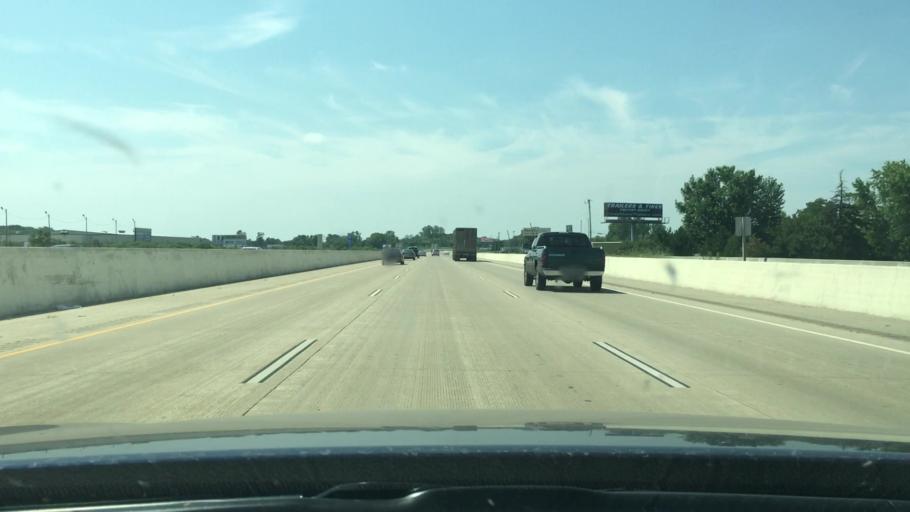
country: US
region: Wisconsin
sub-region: Winnebago County
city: Neenah
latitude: 44.1319
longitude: -88.4962
